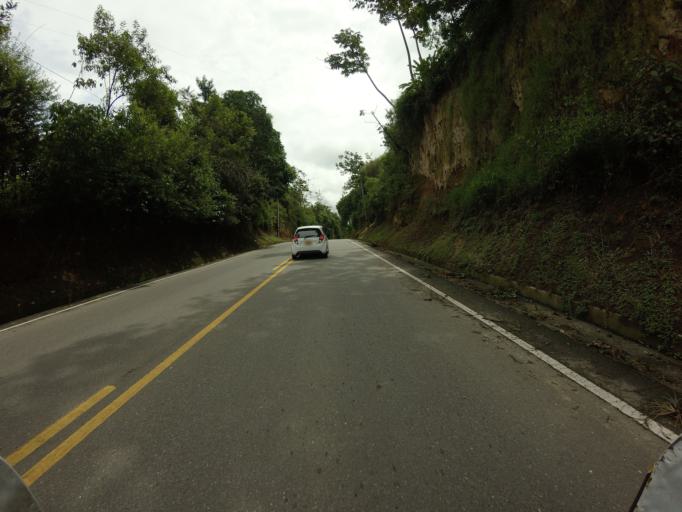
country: CO
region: Valle del Cauca
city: Alcala
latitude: 4.6512
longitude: -75.7744
